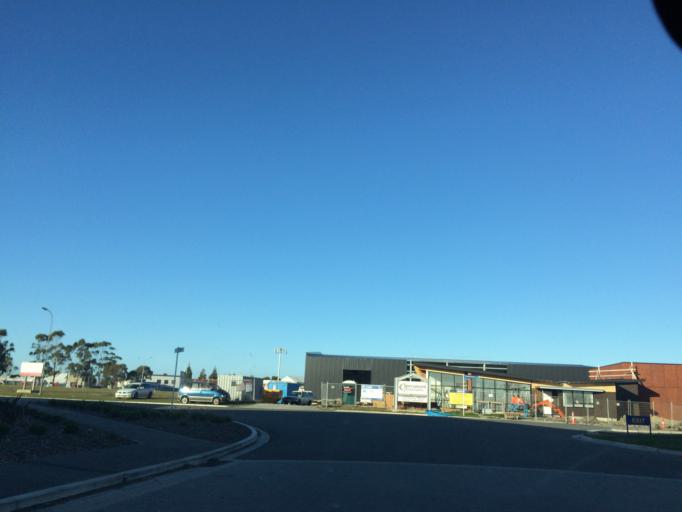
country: NZ
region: Canterbury
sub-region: Selwyn District
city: Prebbleton
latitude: -43.5399
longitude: 172.5469
